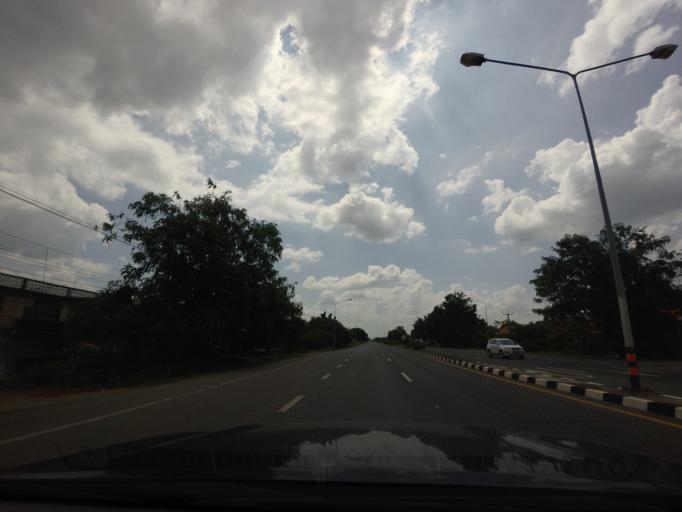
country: TH
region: Phetchabun
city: Nong Phai
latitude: 16.1772
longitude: 101.0830
